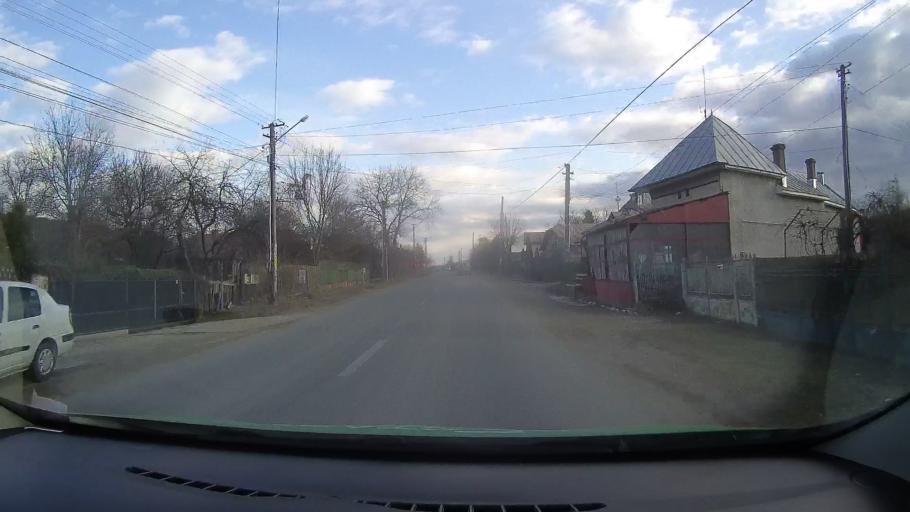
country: RO
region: Dambovita
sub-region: Comuna Gura Ocnitei
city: Gura Ocnitei
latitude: 44.9506
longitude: 25.5572
